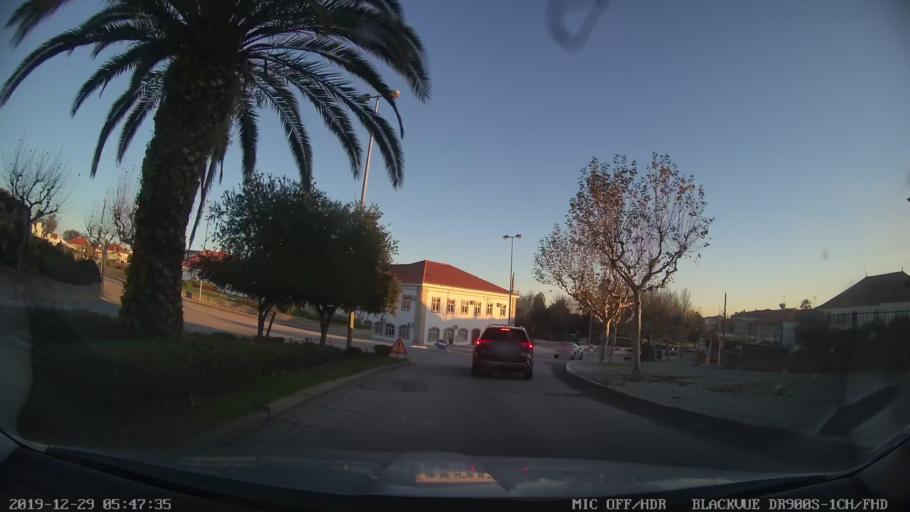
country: PT
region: Castelo Branco
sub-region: Idanha-A-Nova
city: Idanha-a-Nova
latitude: 39.9236
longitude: -7.2425
